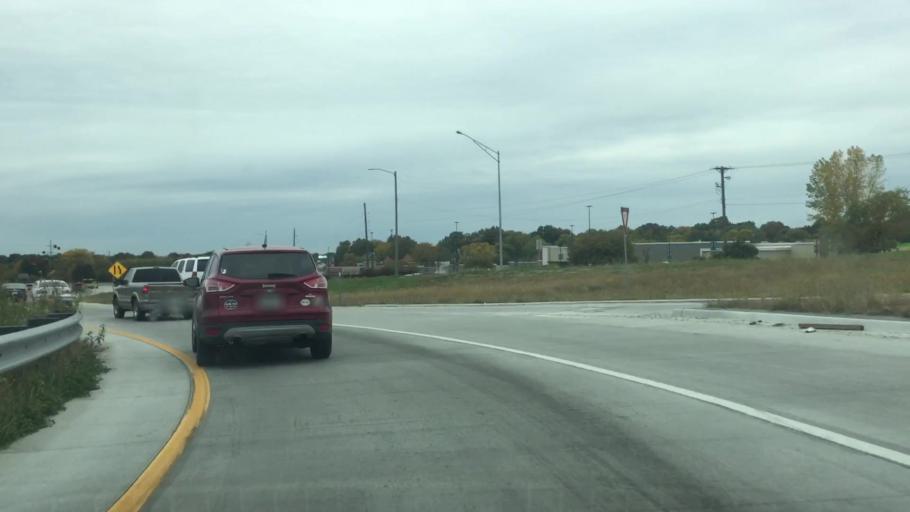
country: US
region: Missouri
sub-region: Jackson County
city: Lees Summit
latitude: 38.9038
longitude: -94.3781
